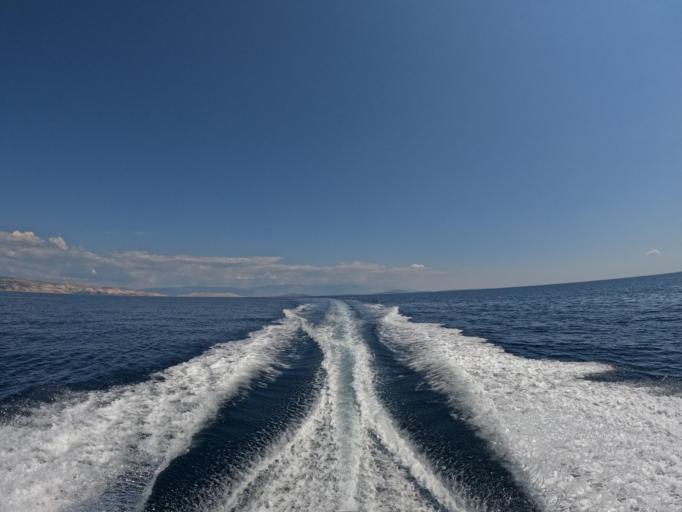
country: HR
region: Primorsko-Goranska
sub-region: Grad Krk
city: Krk
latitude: 44.9305
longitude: 14.5231
